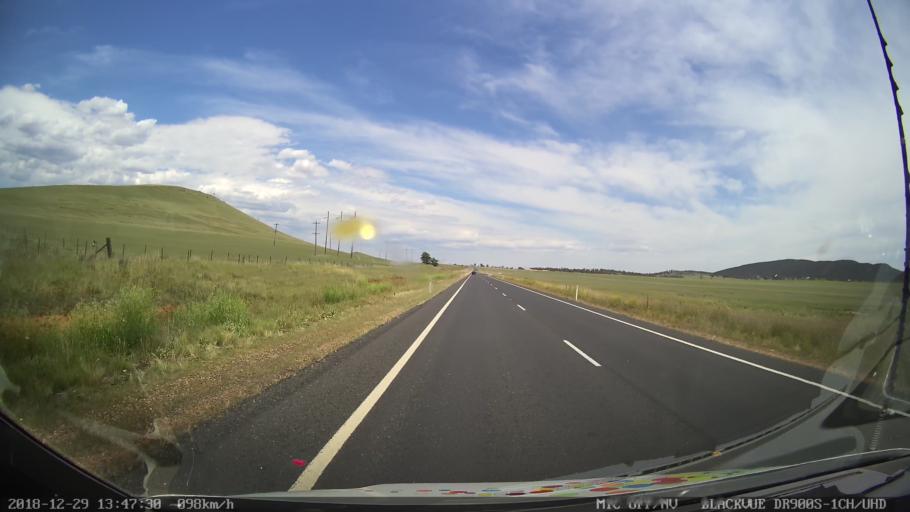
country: AU
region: New South Wales
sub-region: Cooma-Monaro
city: Cooma
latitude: -36.1274
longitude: 149.1431
